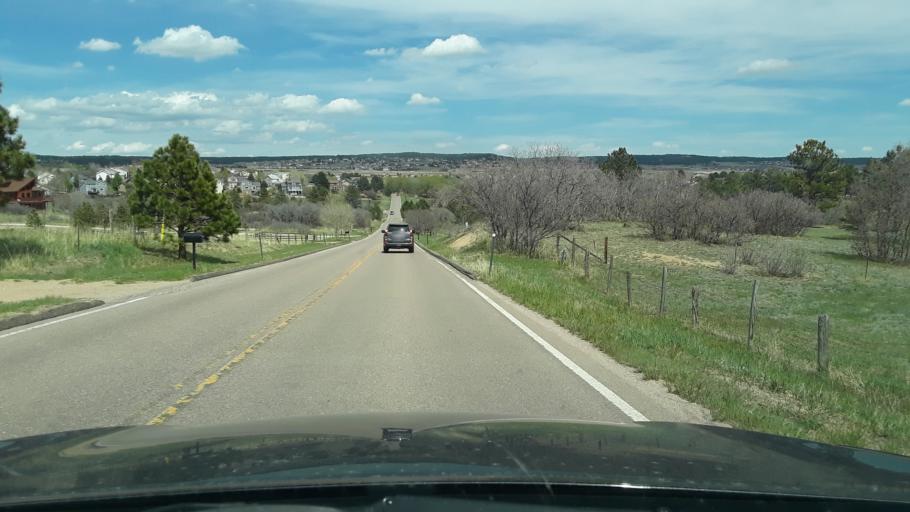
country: US
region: Colorado
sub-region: El Paso County
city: Monument
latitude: 39.0821
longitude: -104.8808
